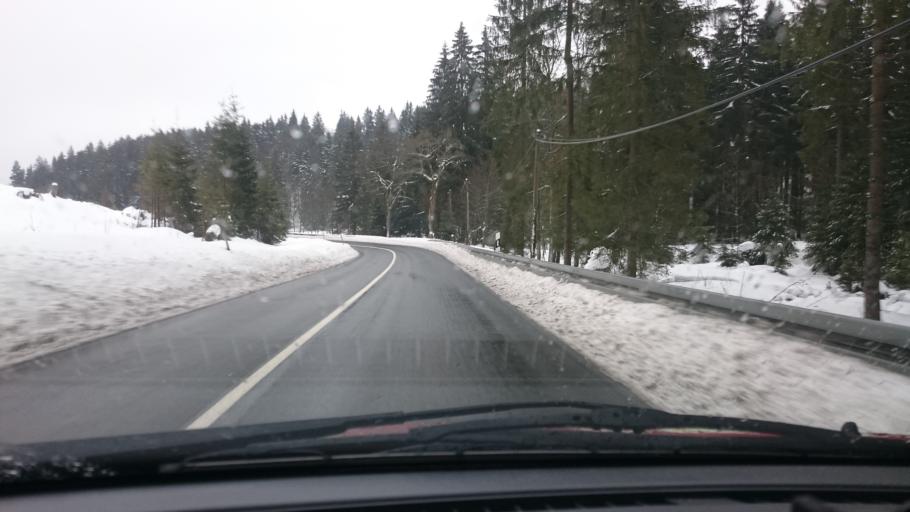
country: DE
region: Saxony
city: Tannenbergsthal
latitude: 50.4164
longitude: 12.4829
